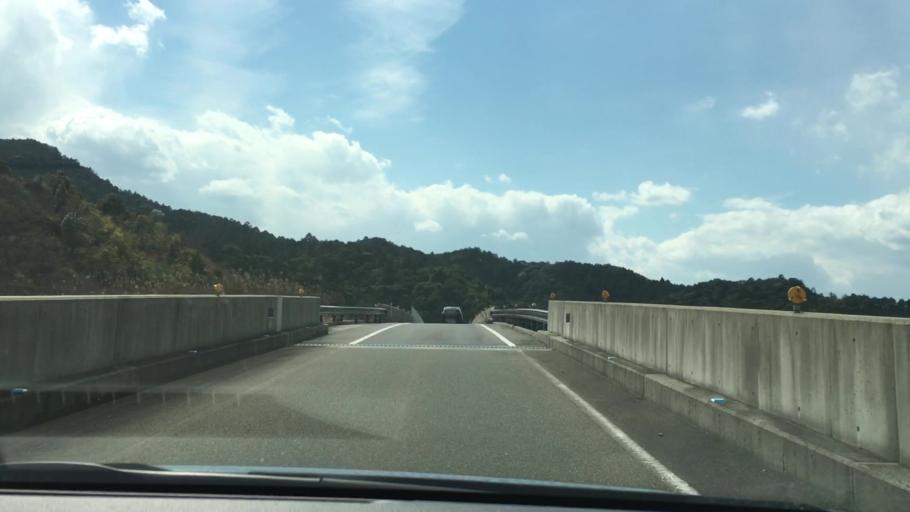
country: JP
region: Mie
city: Toba
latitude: 34.4890
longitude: 136.8029
